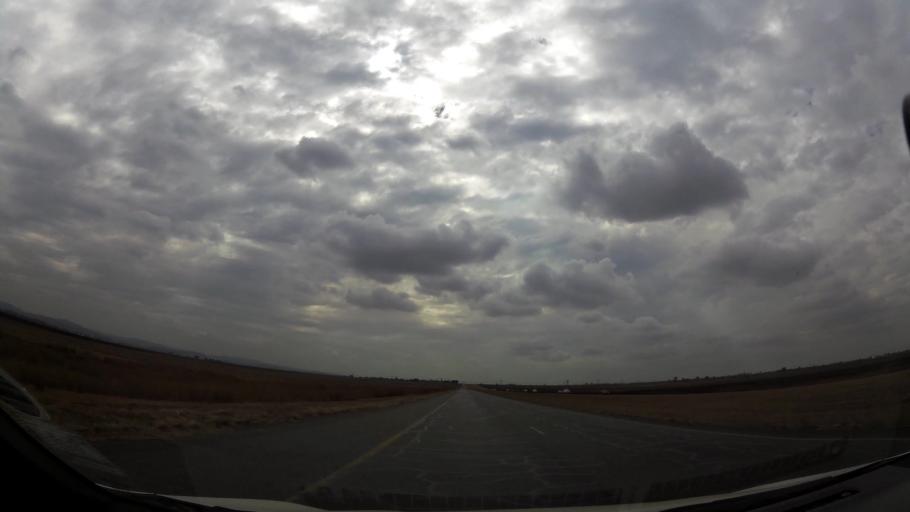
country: ZA
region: Gauteng
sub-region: Ekurhuleni Metropolitan Municipality
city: Germiston
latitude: -26.3756
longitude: 28.0900
